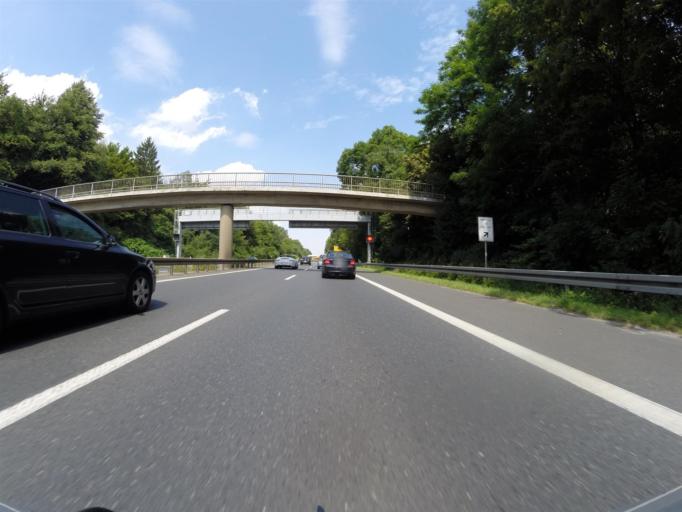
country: DE
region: Lower Saxony
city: Laatzen
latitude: 52.3406
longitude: 9.8024
